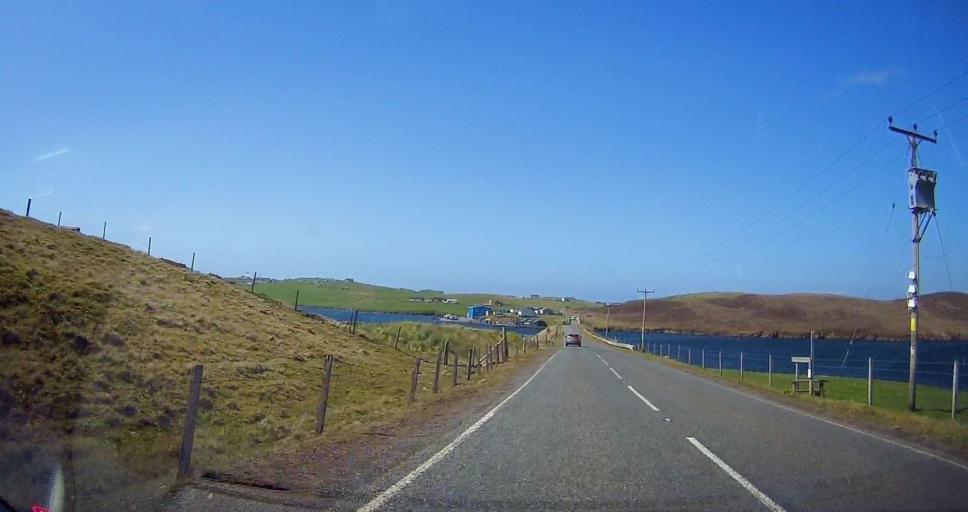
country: GB
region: Scotland
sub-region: Shetland Islands
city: Sandwick
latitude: 60.1061
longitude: -1.3016
